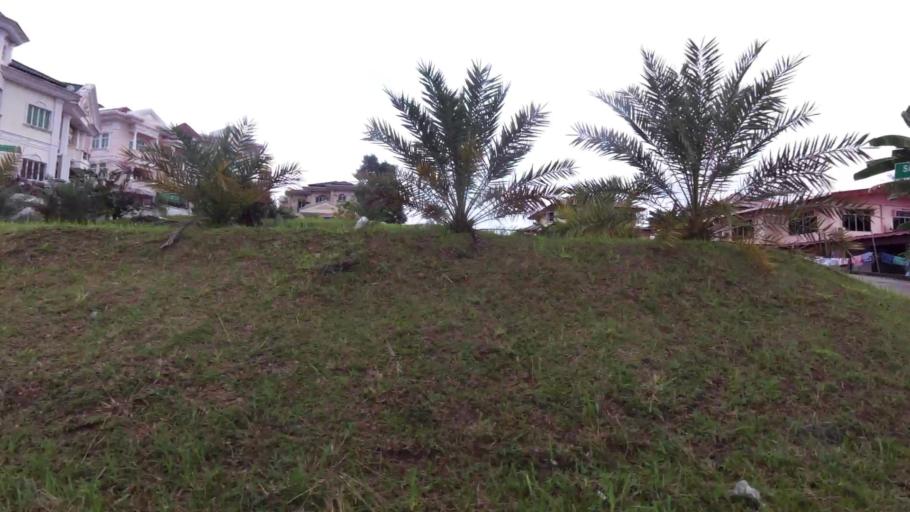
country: BN
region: Brunei and Muara
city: Bandar Seri Begawan
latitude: 4.8980
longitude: 114.9192
